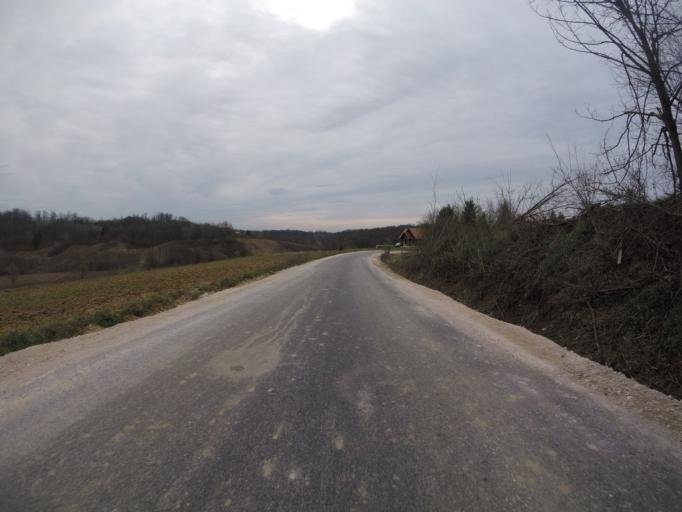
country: HR
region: Grad Zagreb
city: Strmec
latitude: 45.6068
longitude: 15.9101
